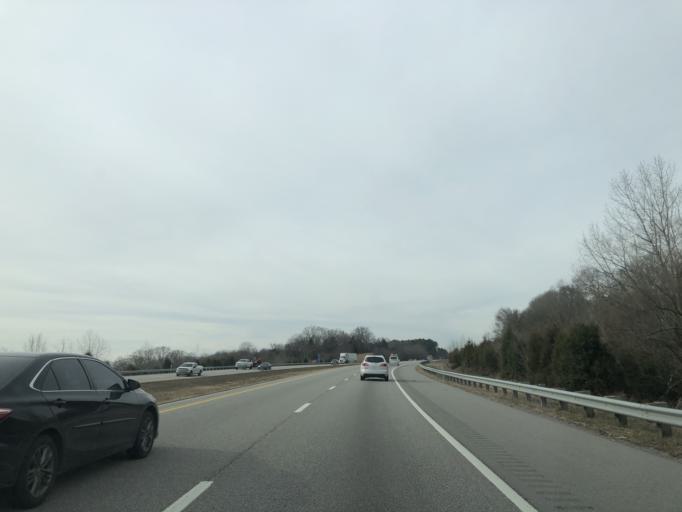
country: US
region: Tennessee
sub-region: Williamson County
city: Nolensville
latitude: 35.8416
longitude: -86.6382
